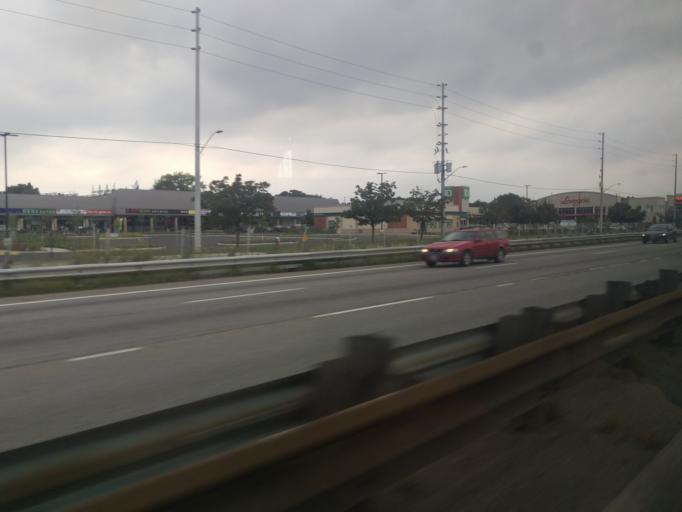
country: CA
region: Ontario
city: Etobicoke
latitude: 43.5906
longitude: -79.5754
